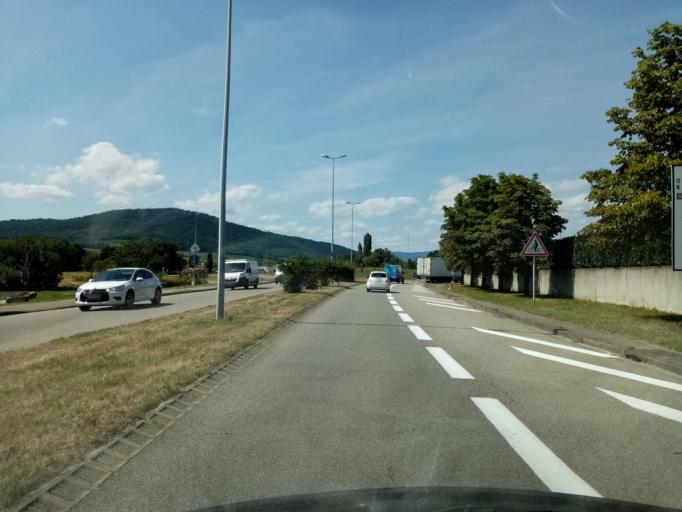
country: FR
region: Alsace
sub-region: Departement du Bas-Rhin
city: Selestat
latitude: 48.2556
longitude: 7.4256
